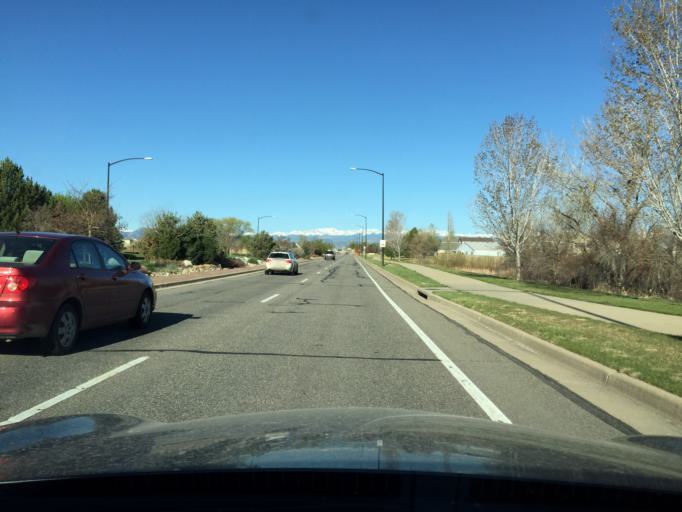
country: US
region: Colorado
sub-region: Boulder County
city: Erie
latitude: 40.0368
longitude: -105.0672
